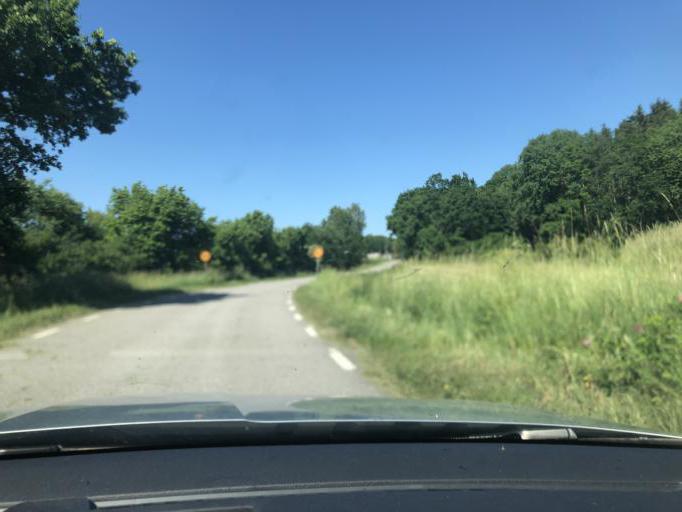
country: SE
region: Blekinge
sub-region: Karlshamns Kommun
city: Morrum
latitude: 56.1875
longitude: 14.6761
